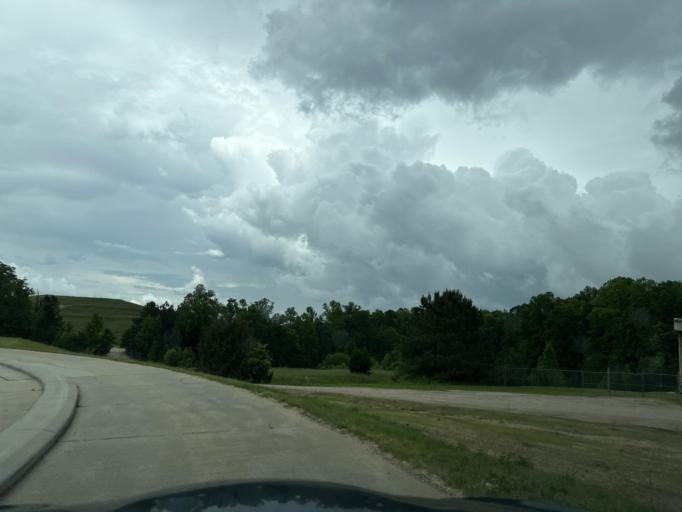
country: US
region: North Carolina
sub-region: Wake County
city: Wake Forest
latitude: 35.9089
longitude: -78.5744
